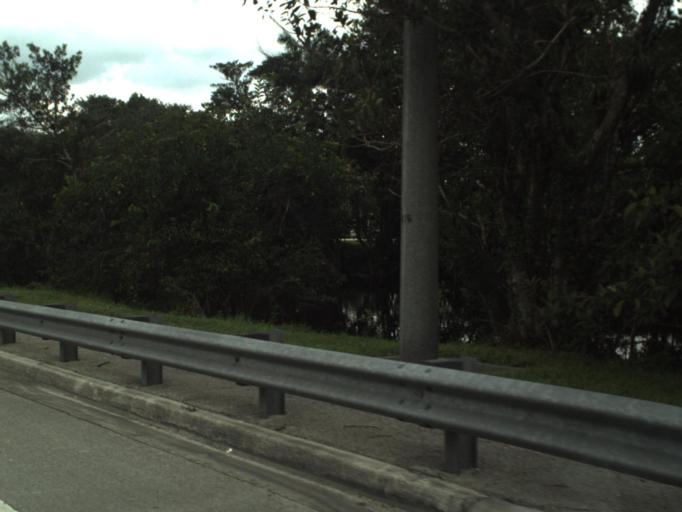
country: US
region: Florida
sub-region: Broward County
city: Cooper City
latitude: 26.0642
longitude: -80.2856
